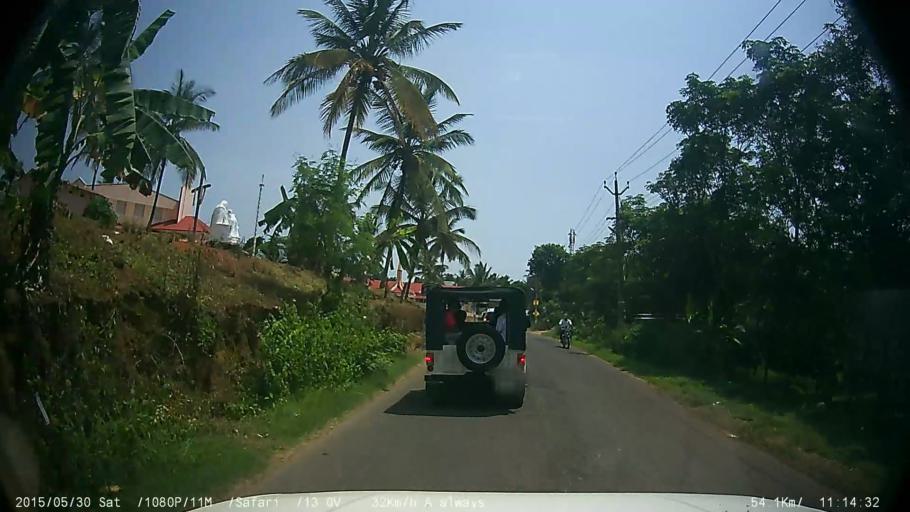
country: IN
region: Kerala
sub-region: Wayanad
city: Panamaram
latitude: 11.7670
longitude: 76.0611
